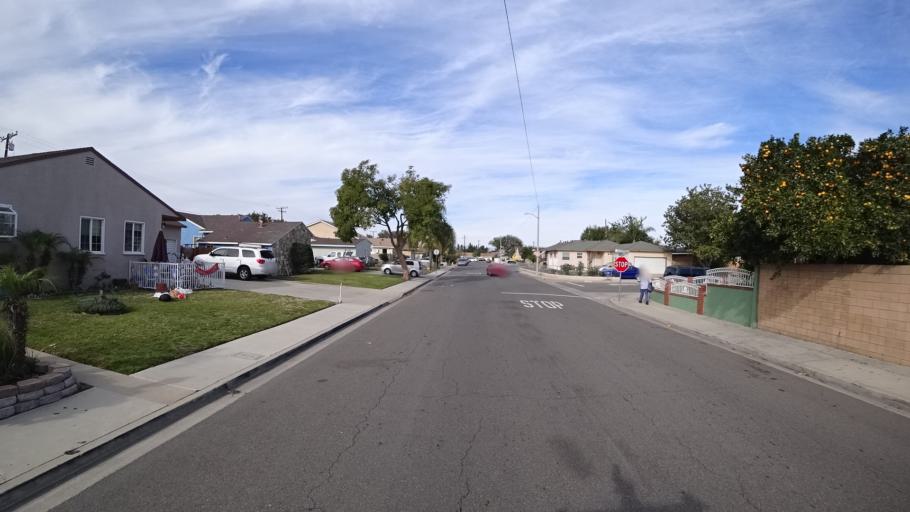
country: US
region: California
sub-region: Orange County
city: Garden Grove
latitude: 33.7693
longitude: -117.9069
